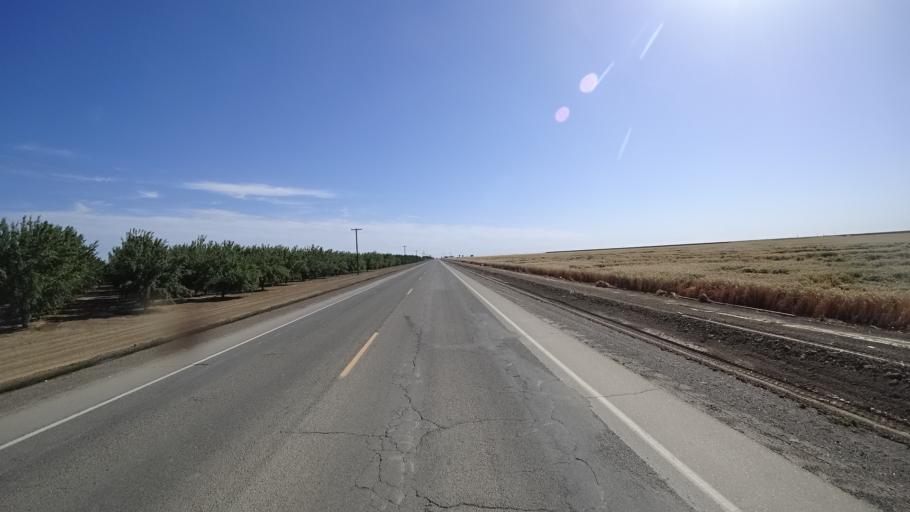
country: US
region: California
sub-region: Kings County
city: Lemoore Station
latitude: 36.1686
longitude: -119.9720
